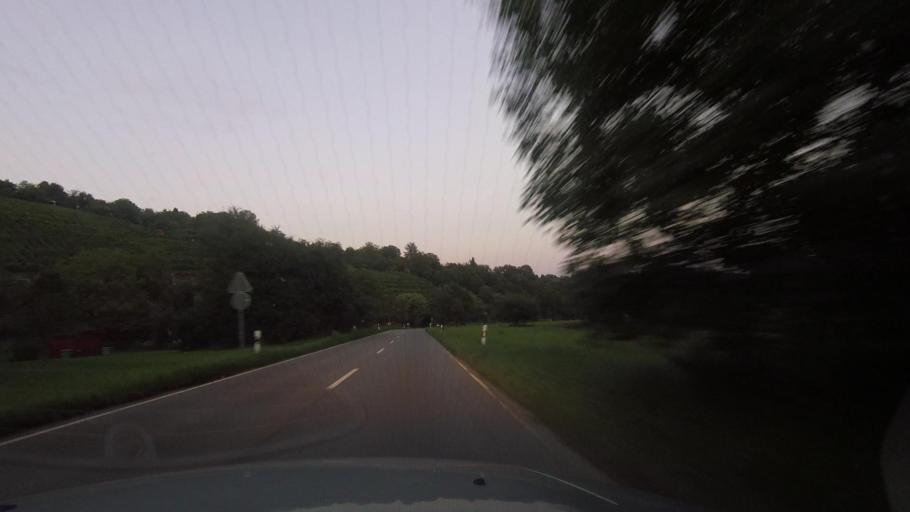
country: DE
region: Baden-Wuerttemberg
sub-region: Regierungsbezirk Stuttgart
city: Benningen am Neckar
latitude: 48.9493
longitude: 9.2446
